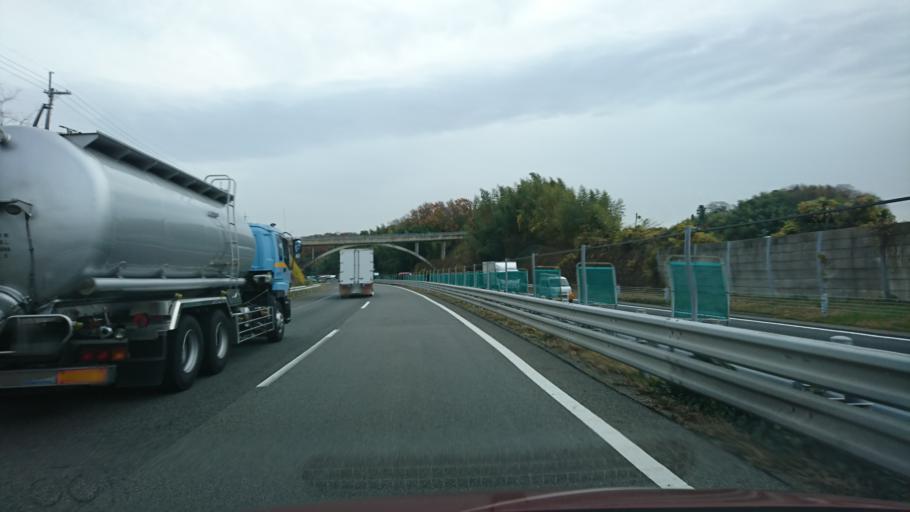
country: JP
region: Hyogo
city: Sandacho
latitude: 34.8269
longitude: 135.1753
